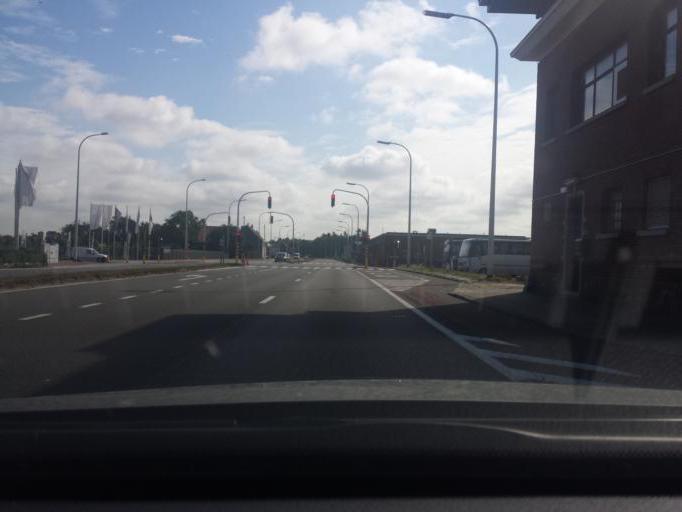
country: BE
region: Flanders
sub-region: Provincie Vlaams-Brabant
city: Zaventem
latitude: 50.9098
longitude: 4.4767
